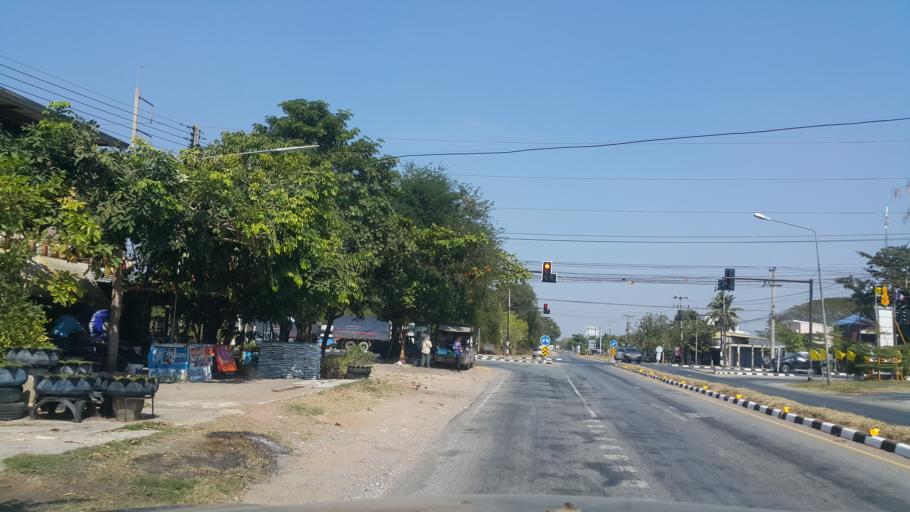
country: TH
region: Nakhon Ratchasima
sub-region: Amphoe Kaeng Sanam Nang
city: Kaeng Sanam Nang
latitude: 15.6893
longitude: 102.3322
